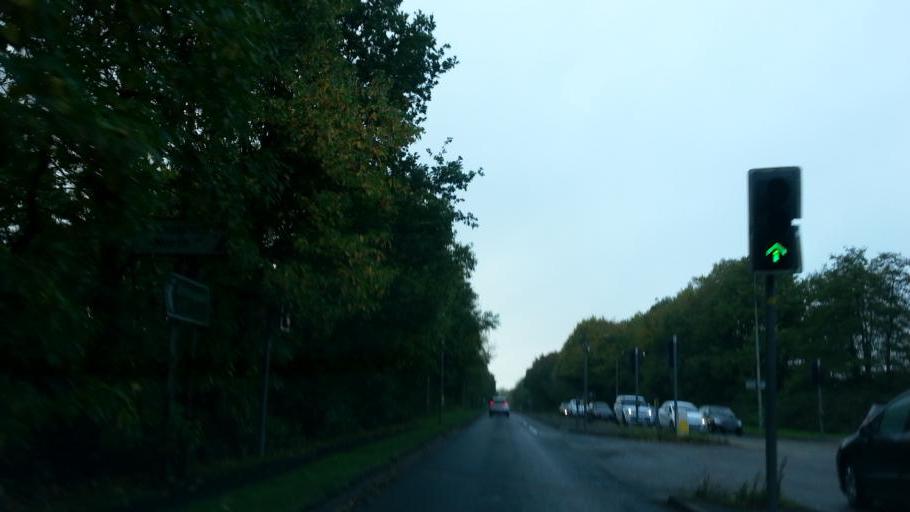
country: GB
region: England
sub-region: Worcestershire
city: Bromsgrove
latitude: 52.3483
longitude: -2.0480
